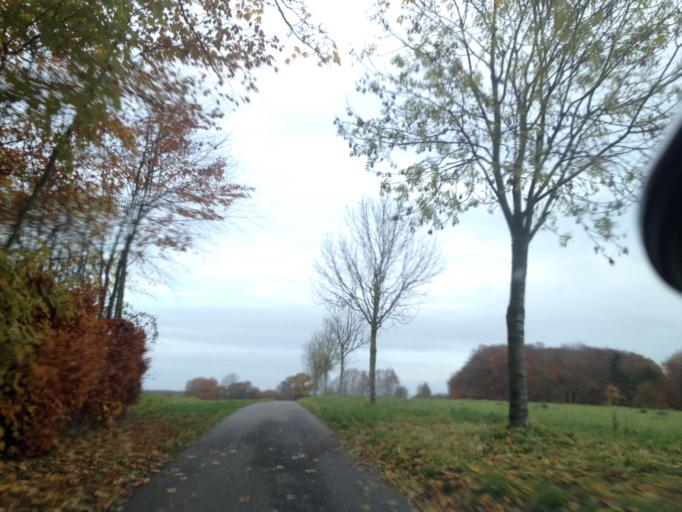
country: DK
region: South Denmark
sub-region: Assens Kommune
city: Vissenbjerg
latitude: 55.4310
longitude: 10.1659
